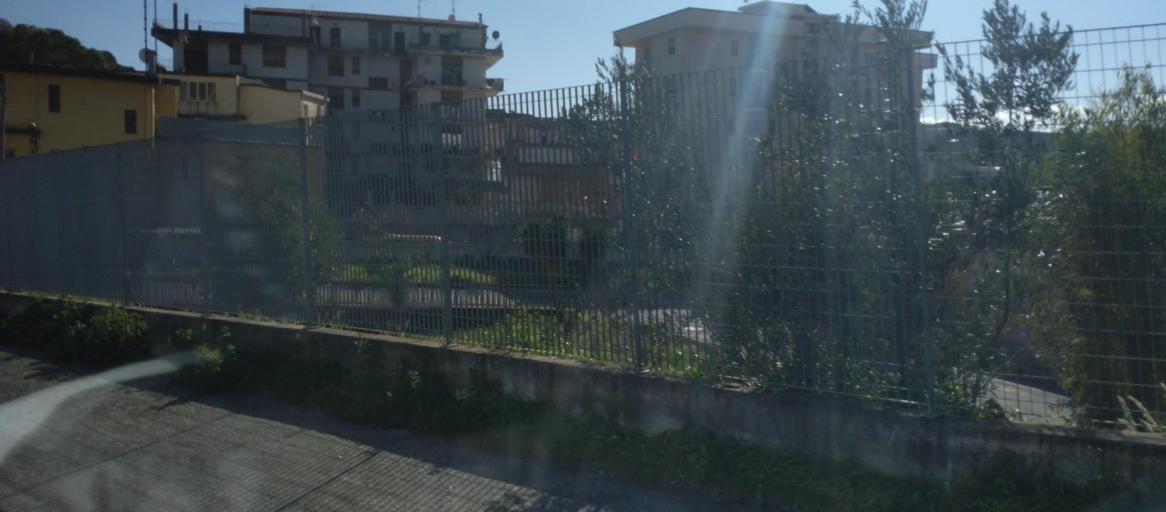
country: IT
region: Calabria
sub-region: Provincia di Catanzaro
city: Catanzaro
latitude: 38.8962
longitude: 16.6017
